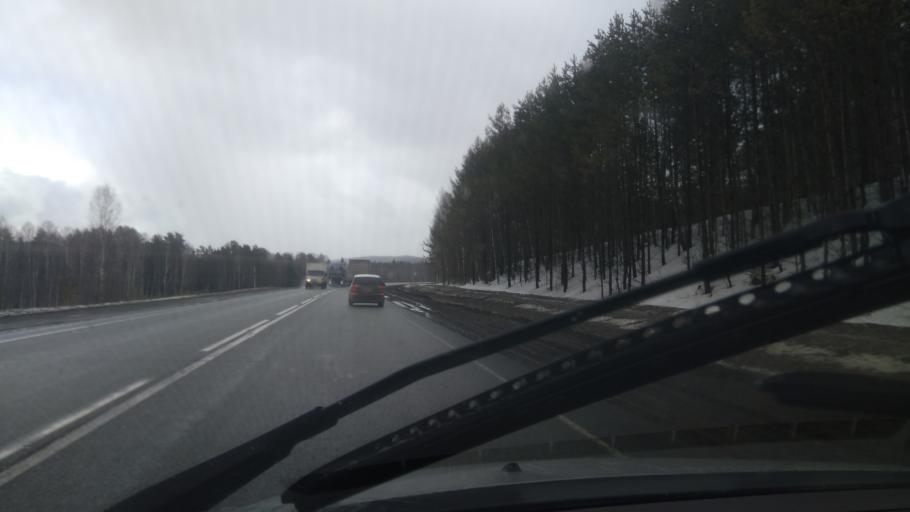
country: RU
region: Sverdlovsk
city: Ufimskiy
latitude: 56.7862
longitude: 58.3879
